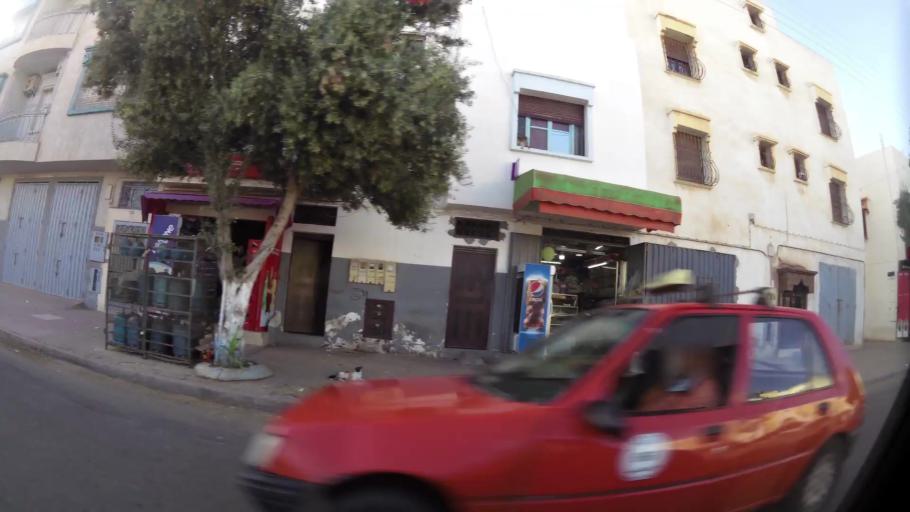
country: MA
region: Oued ed Dahab-Lagouira
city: Dakhla
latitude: 30.3967
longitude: -9.5453
